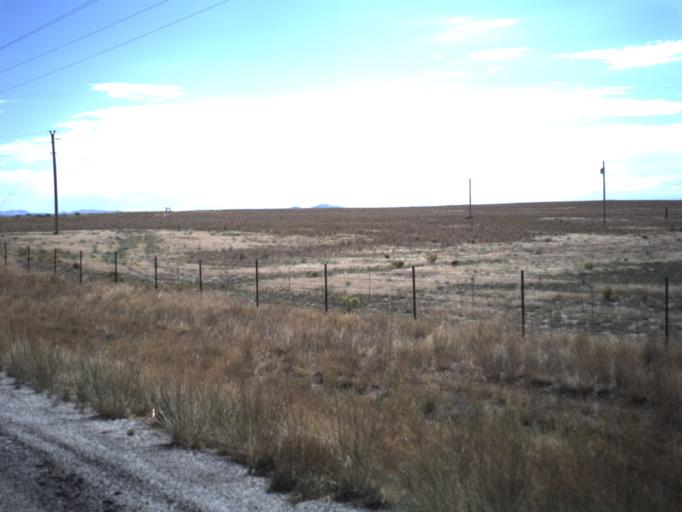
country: US
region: Idaho
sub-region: Oneida County
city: Malad City
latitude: 41.9651
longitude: -113.0608
